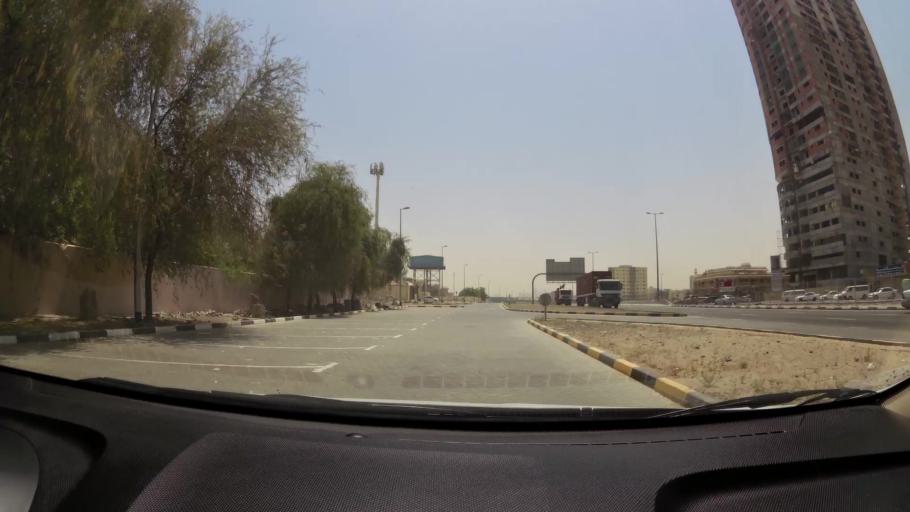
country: AE
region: Ajman
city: Ajman
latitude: 25.3993
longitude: 55.5116
